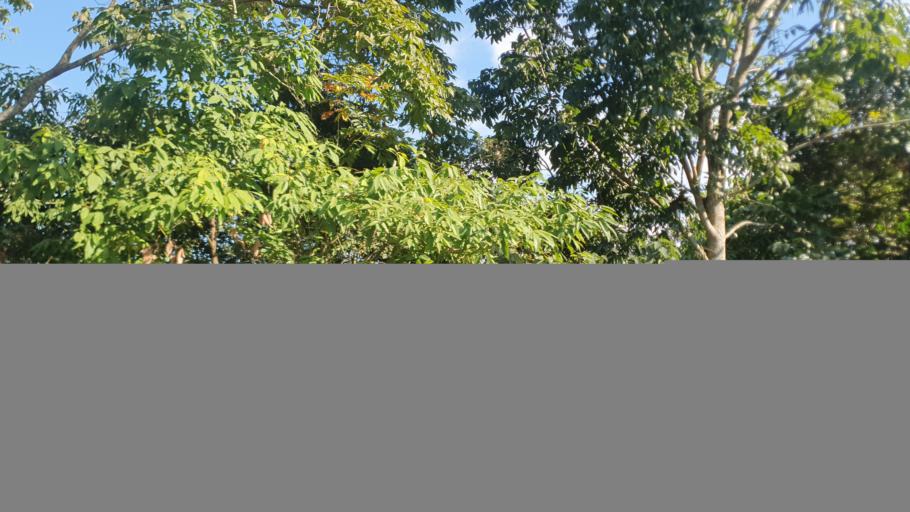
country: TW
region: Taiwan
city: Yujing
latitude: 23.0209
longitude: 120.3842
